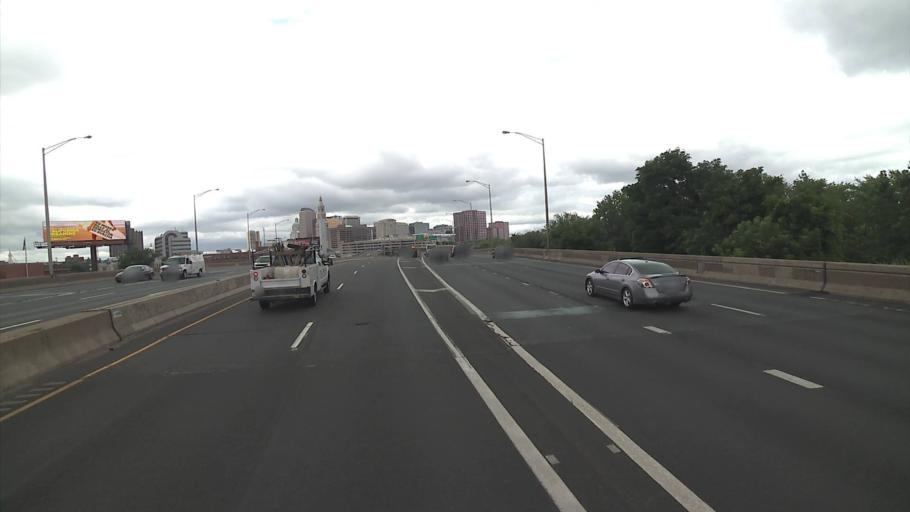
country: US
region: Connecticut
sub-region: Hartford County
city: Hartford
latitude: 41.7574
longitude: -72.6628
